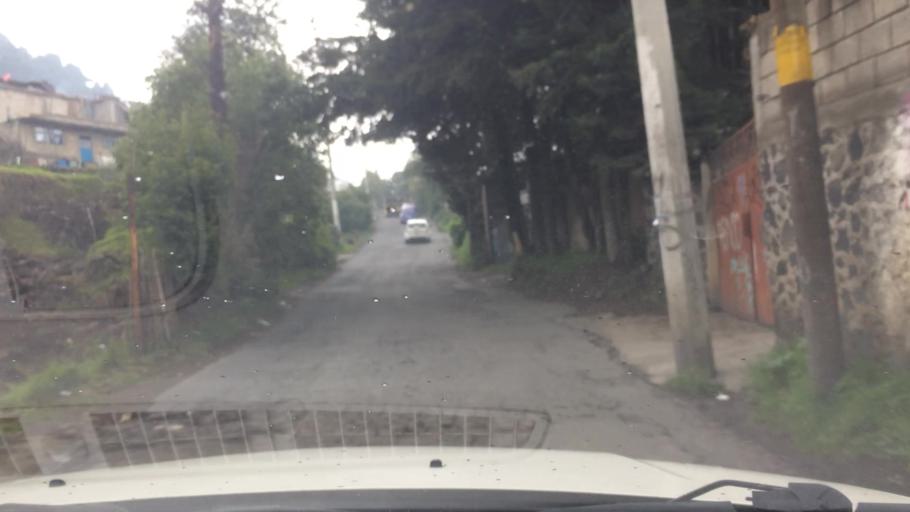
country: MX
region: Mexico City
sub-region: Tlalpan
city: Lomas de Tepemecatl
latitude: 19.2251
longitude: -99.2100
